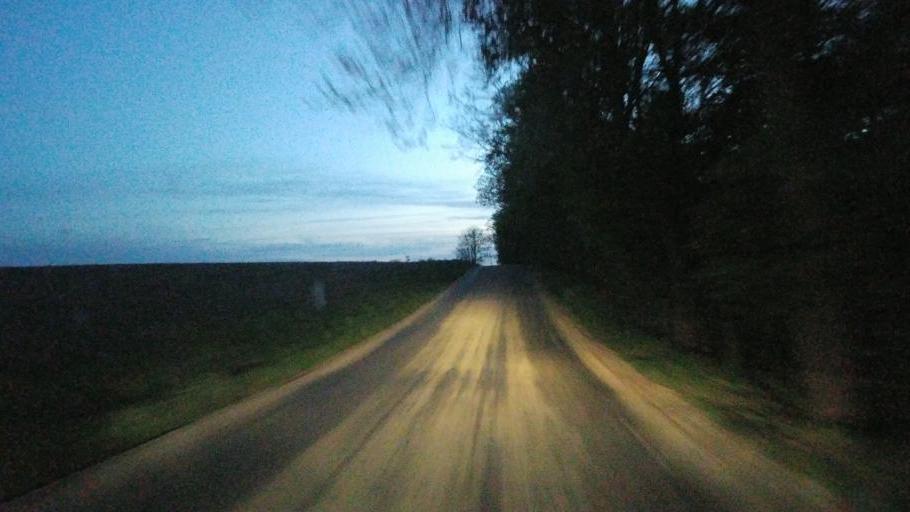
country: US
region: Ohio
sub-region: Knox County
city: Danville
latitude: 40.5211
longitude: -82.3818
